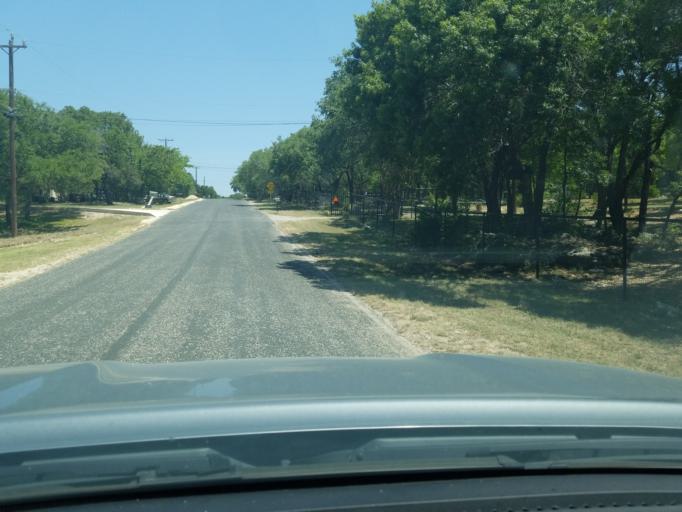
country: US
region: Texas
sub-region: Bexar County
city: Timberwood Park
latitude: 29.7198
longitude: -98.4923
